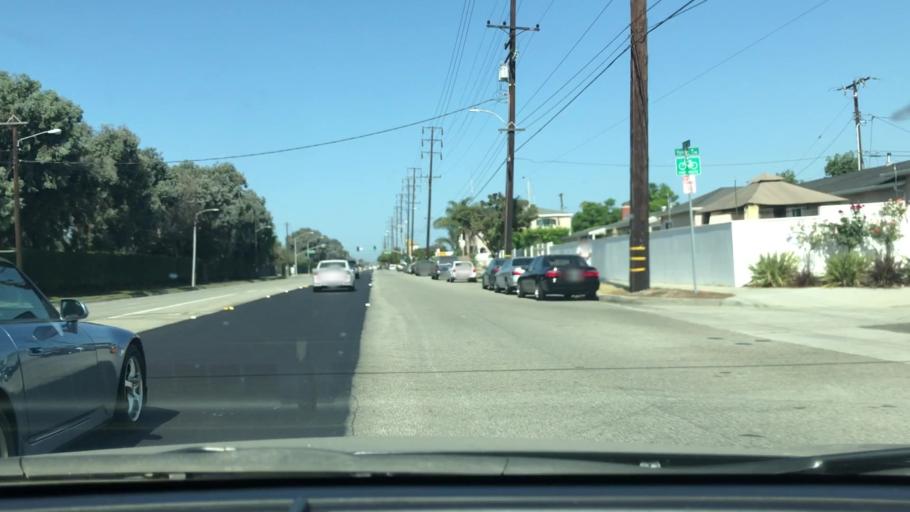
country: US
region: California
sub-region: Los Angeles County
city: Torrance
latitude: 33.8584
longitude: -118.3351
